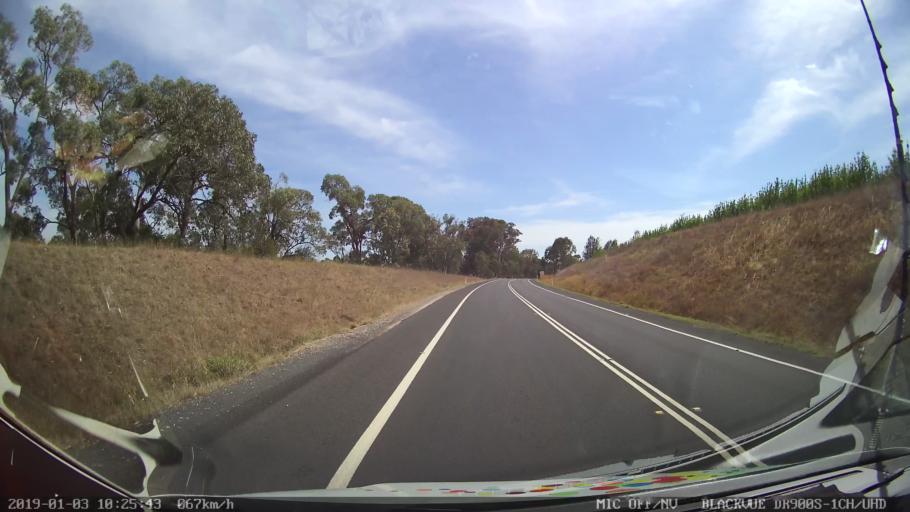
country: AU
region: New South Wales
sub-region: Young
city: Young
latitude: -34.4203
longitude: 148.2442
